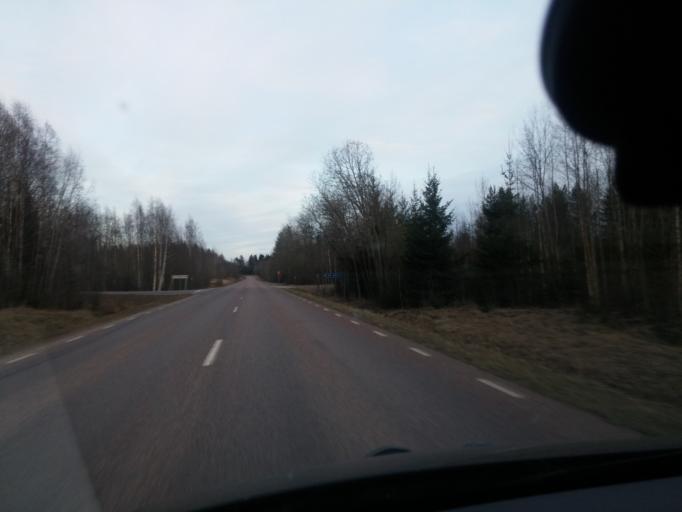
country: SE
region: Dalarna
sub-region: Faluns Kommun
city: Bjursas
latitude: 60.7272
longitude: 15.4315
